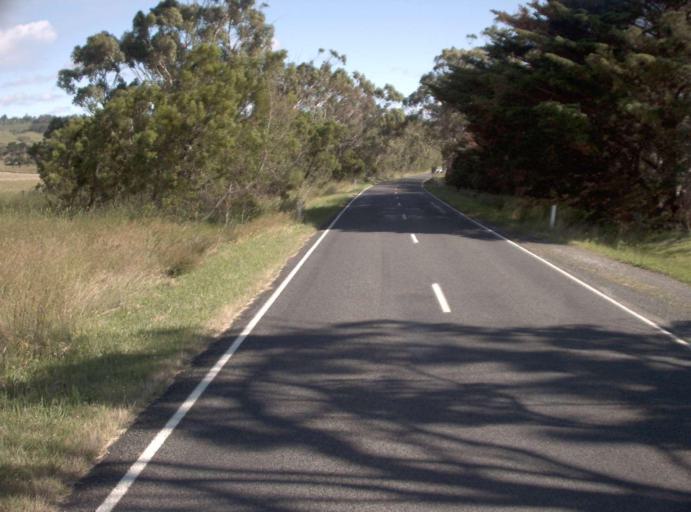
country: AU
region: Victoria
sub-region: Latrobe
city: Traralgon
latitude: -38.1592
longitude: 146.4922
